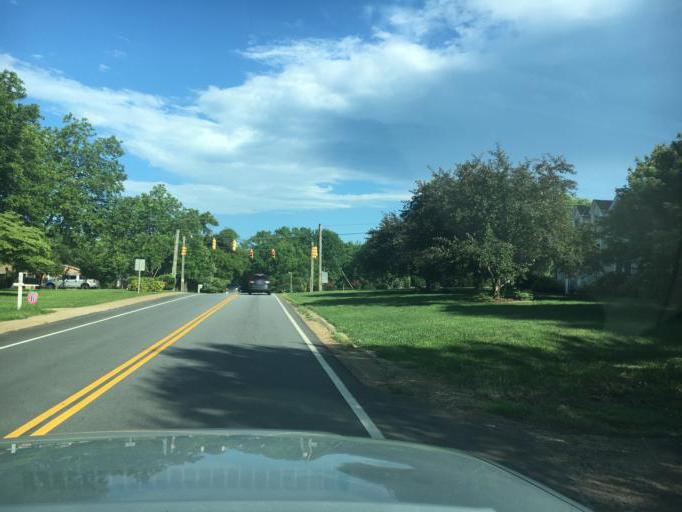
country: US
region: South Carolina
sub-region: Greenville County
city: Mauldin
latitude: 34.7821
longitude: -82.2925
